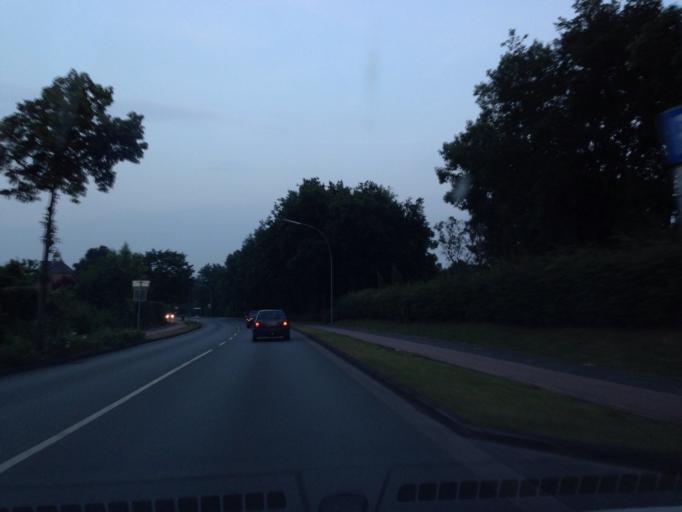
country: DE
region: North Rhine-Westphalia
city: Ludinghausen
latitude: 51.7676
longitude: 7.4536
